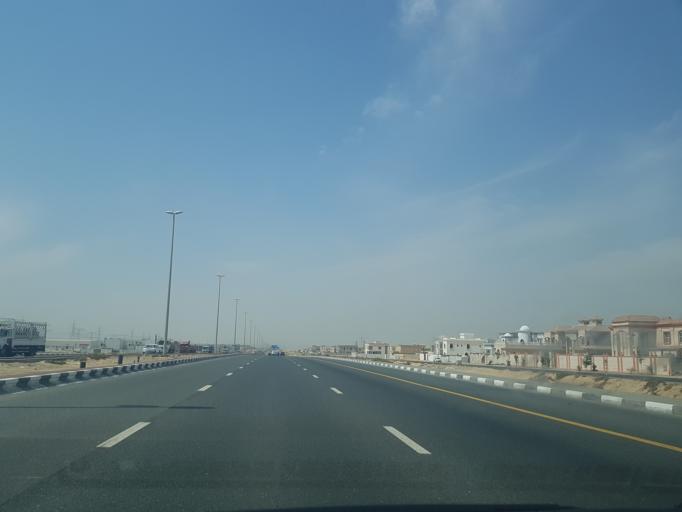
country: AE
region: Ash Shariqah
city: Sharjah
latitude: 25.2625
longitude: 55.5031
